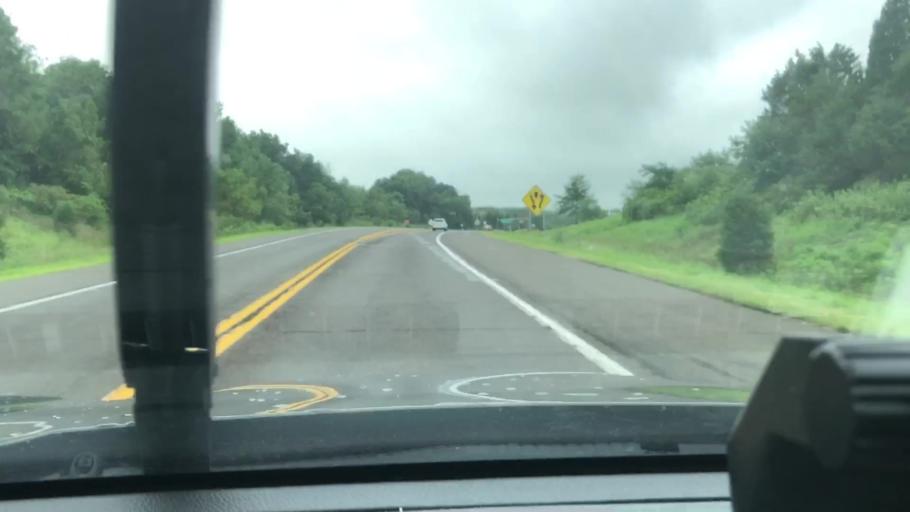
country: US
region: Pennsylvania
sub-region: Bucks County
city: Spinnerstown
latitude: 40.4317
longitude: -75.4330
